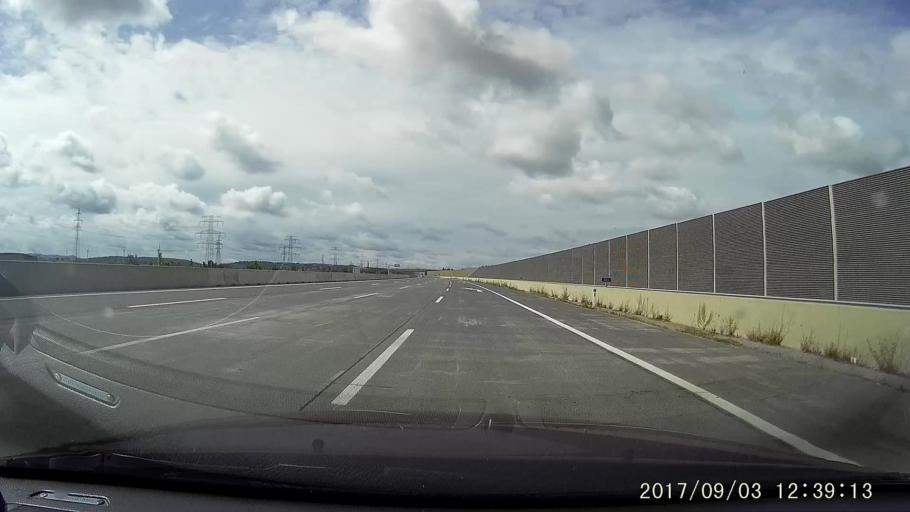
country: AT
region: Lower Austria
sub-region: Politischer Bezirk Mistelbach
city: Grossebersdorf
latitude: 48.3483
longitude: 16.4690
